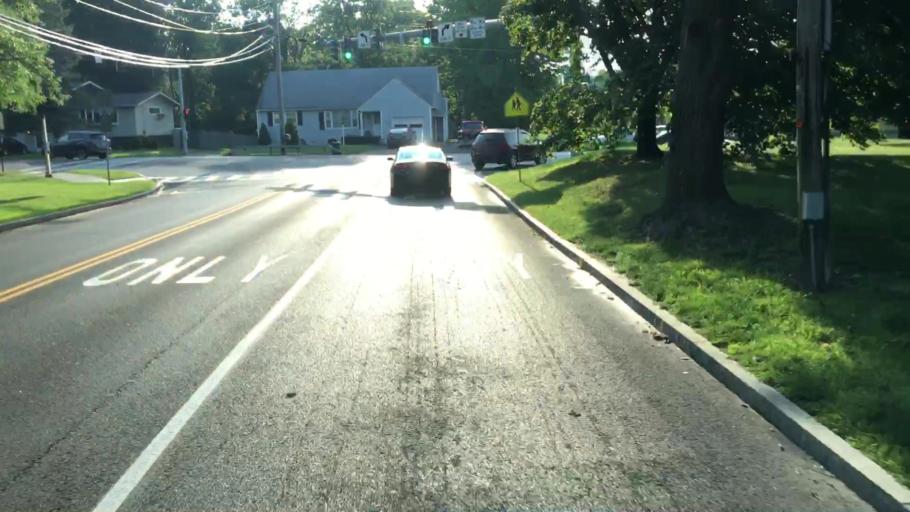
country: US
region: New York
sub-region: Onondaga County
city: Mattydale
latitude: 43.1123
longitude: -76.1593
